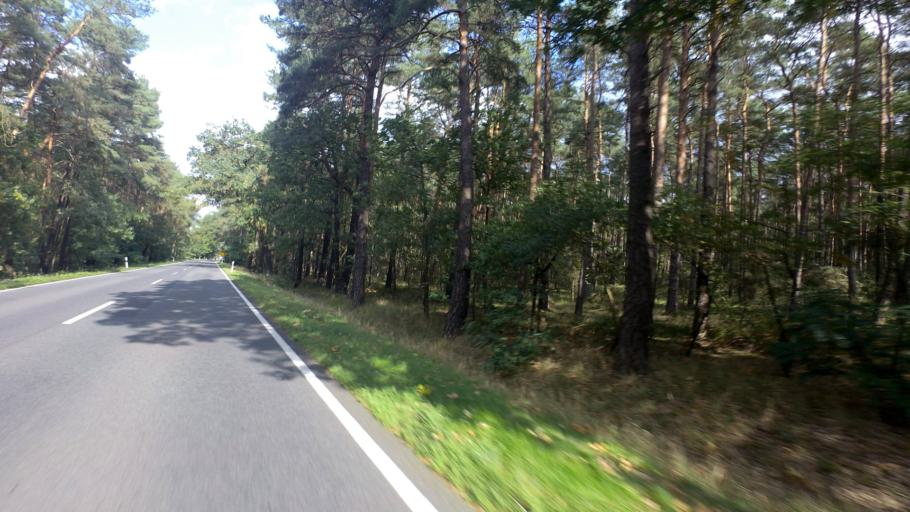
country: DE
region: Brandenburg
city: Herzberg
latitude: 51.7441
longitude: 13.2050
